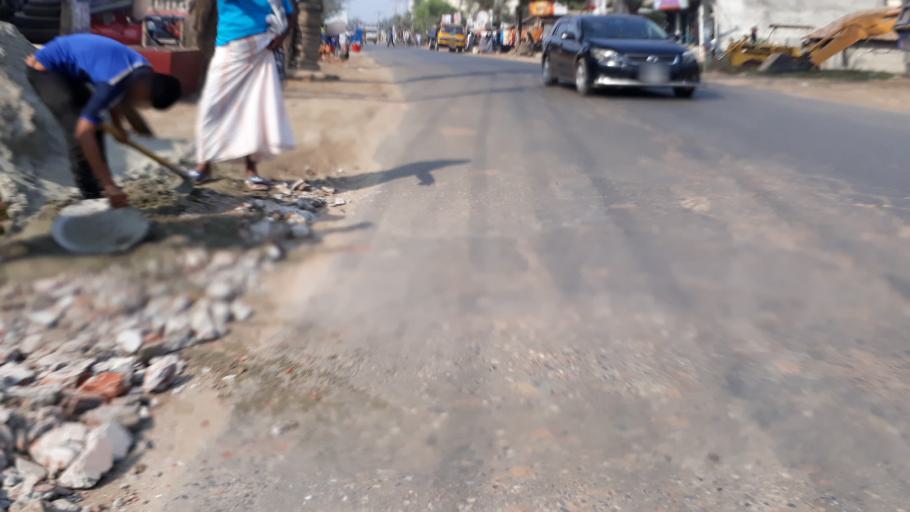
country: BD
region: Dhaka
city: Tungi
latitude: 23.9046
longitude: 90.3242
